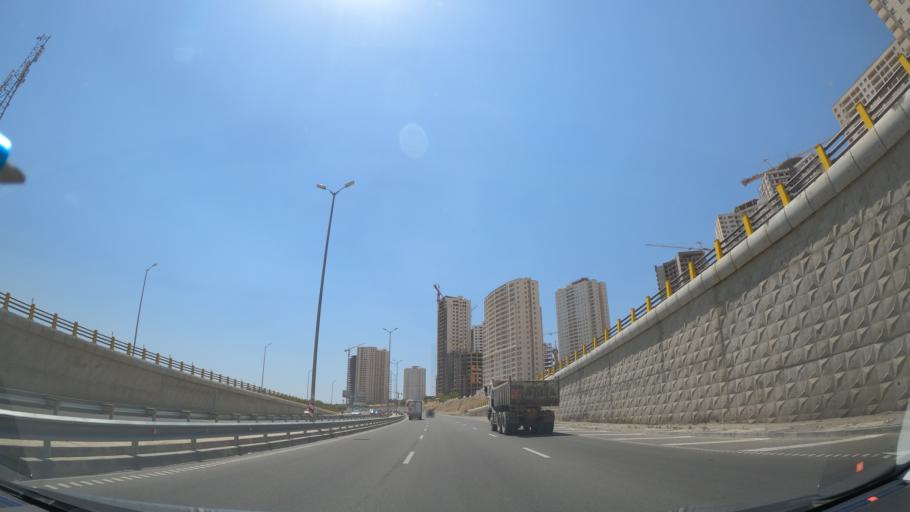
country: IR
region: Tehran
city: Shahr-e Qods
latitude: 35.7523
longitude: 51.1426
